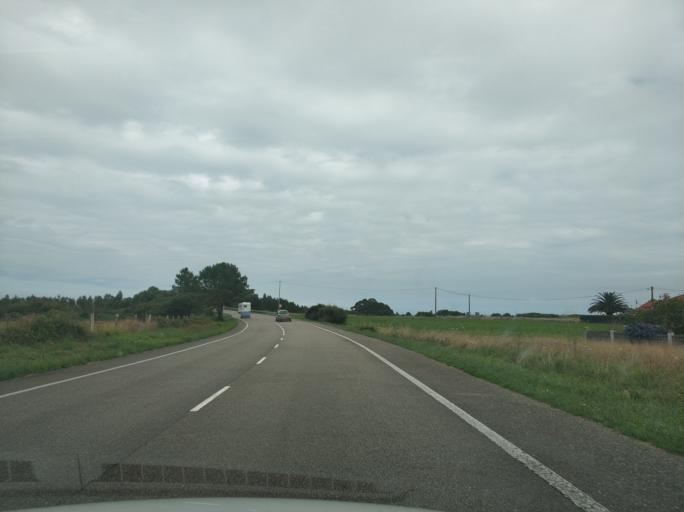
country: ES
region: Asturias
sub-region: Province of Asturias
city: Cudillero
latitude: 43.5620
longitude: -6.1598
